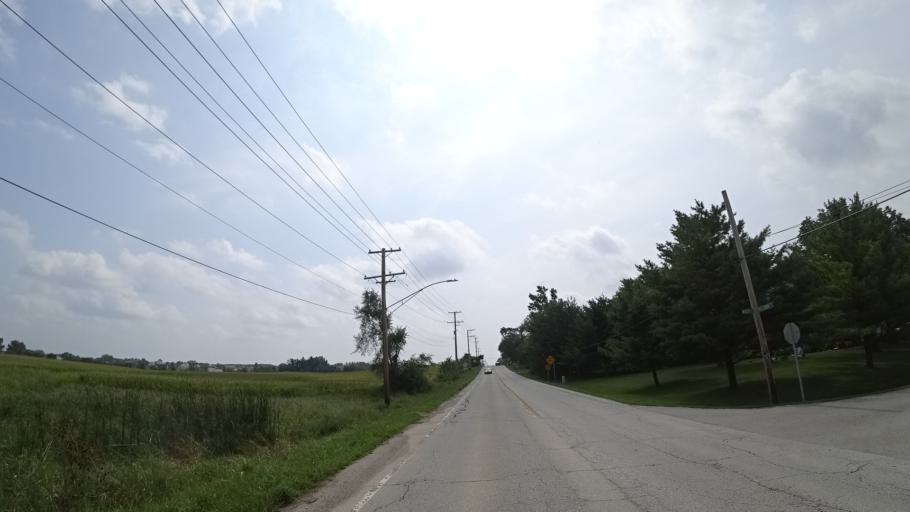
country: US
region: Illinois
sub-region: Will County
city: Goodings Grove
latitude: 41.6178
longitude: -87.9111
